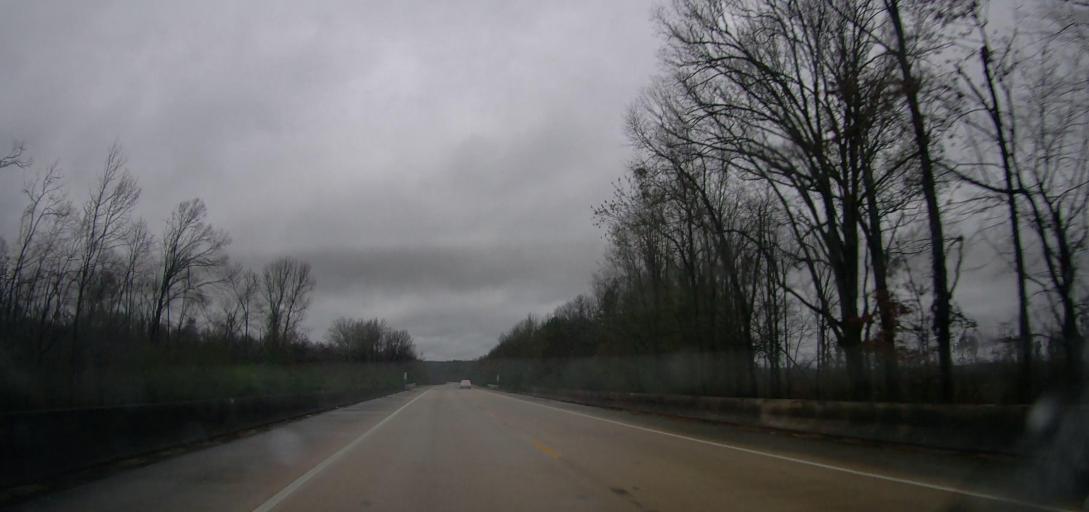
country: US
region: Alabama
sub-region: Chilton County
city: Thorsby
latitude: 32.7569
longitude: -86.8721
